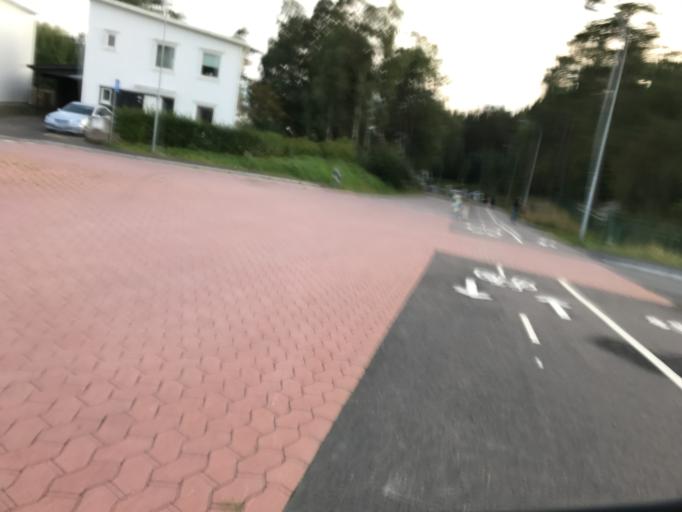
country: SE
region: Vaestra Goetaland
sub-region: Goteborg
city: Majorna
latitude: 57.7203
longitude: 11.8875
